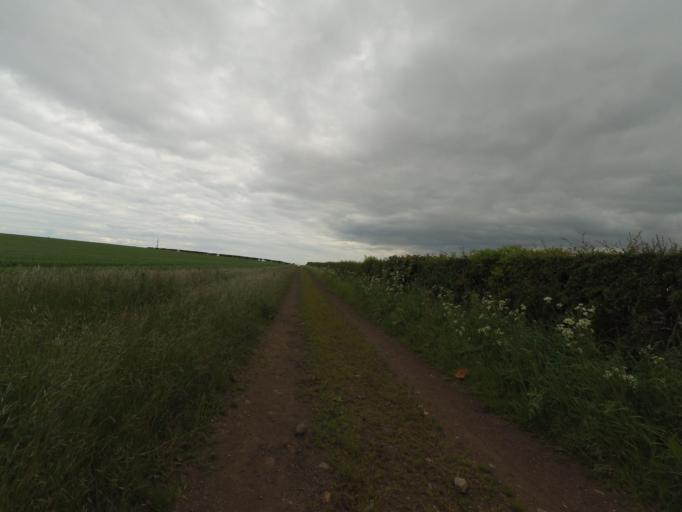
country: GB
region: Scotland
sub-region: East Lothian
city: Prestonpans
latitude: 55.9214
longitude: -2.9936
